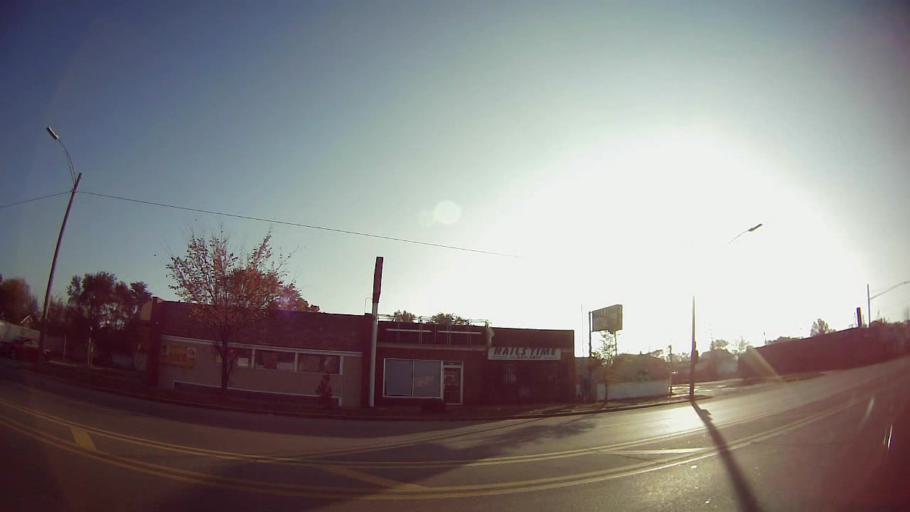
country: US
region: Michigan
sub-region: Wayne County
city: Dearborn
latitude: 42.3592
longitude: -83.1971
